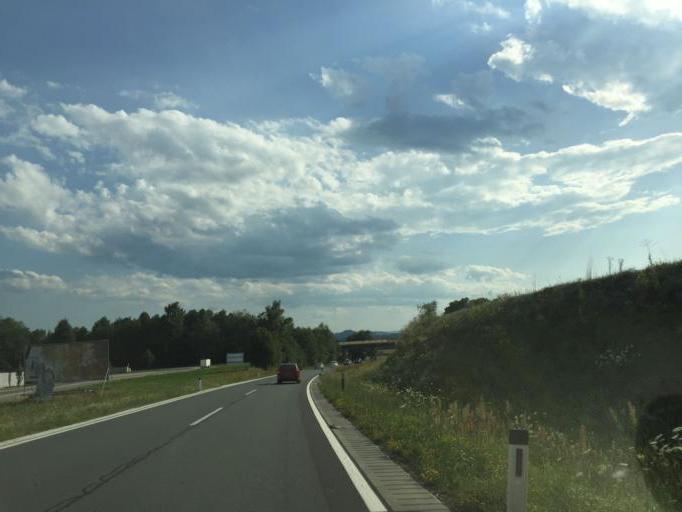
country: AT
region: Styria
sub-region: Politischer Bezirk Leibnitz
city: Sankt Veit am Vogau
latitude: 46.7494
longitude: 15.6234
